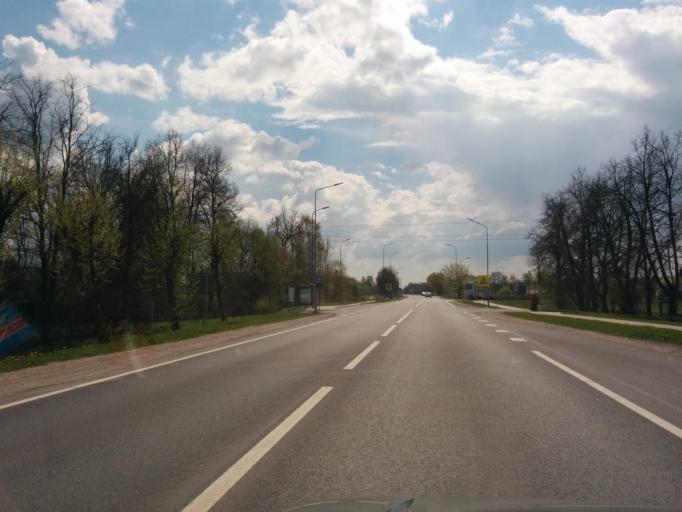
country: LV
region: Jelgava
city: Jelgava
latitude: 56.6265
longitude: 23.7252
